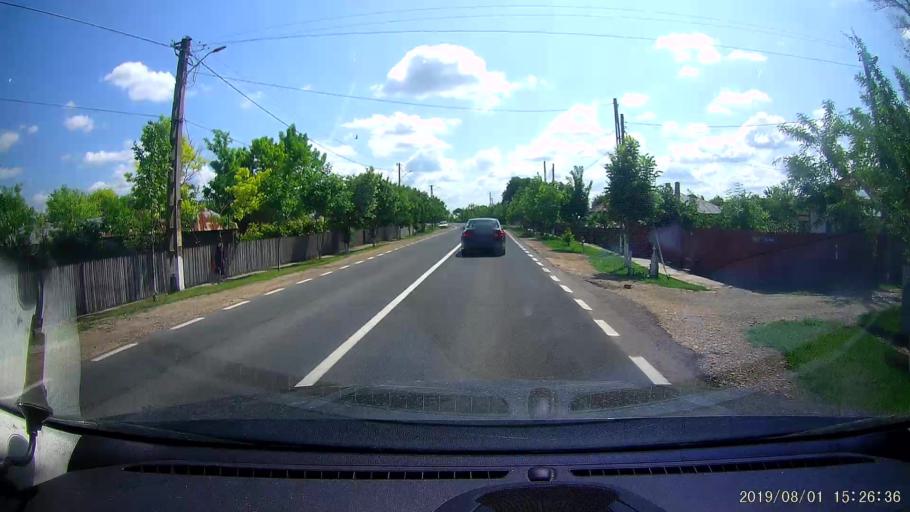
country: RO
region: Braila
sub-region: Comuna Viziru
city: Viziru
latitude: 45.0081
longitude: 27.7192
